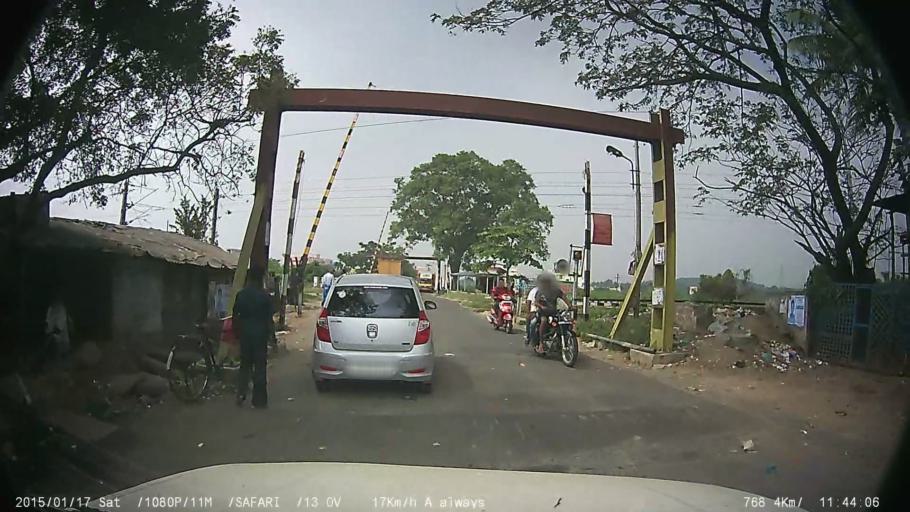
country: IN
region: Tamil Nadu
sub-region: Kancheepuram
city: Singapperumalkovil
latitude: 12.7638
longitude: 80.0025
